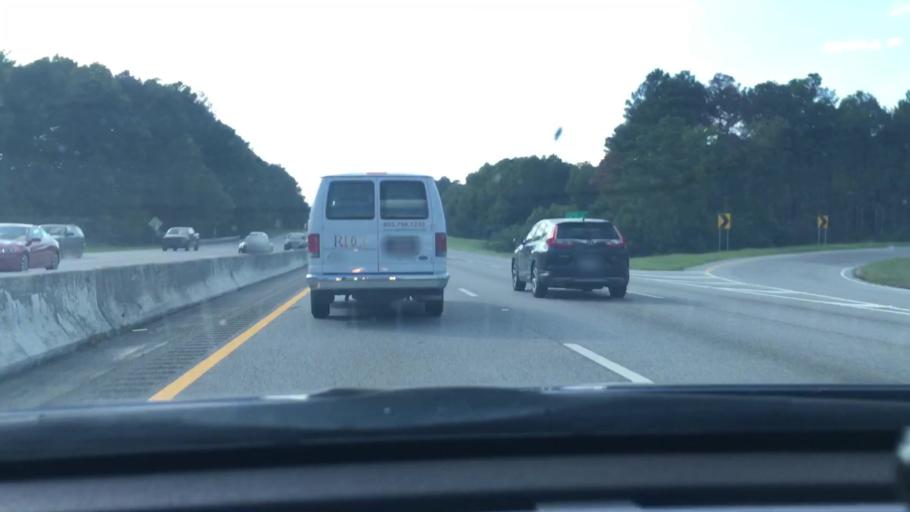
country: US
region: South Carolina
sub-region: Richland County
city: Dentsville
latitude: 34.0737
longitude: -80.9999
